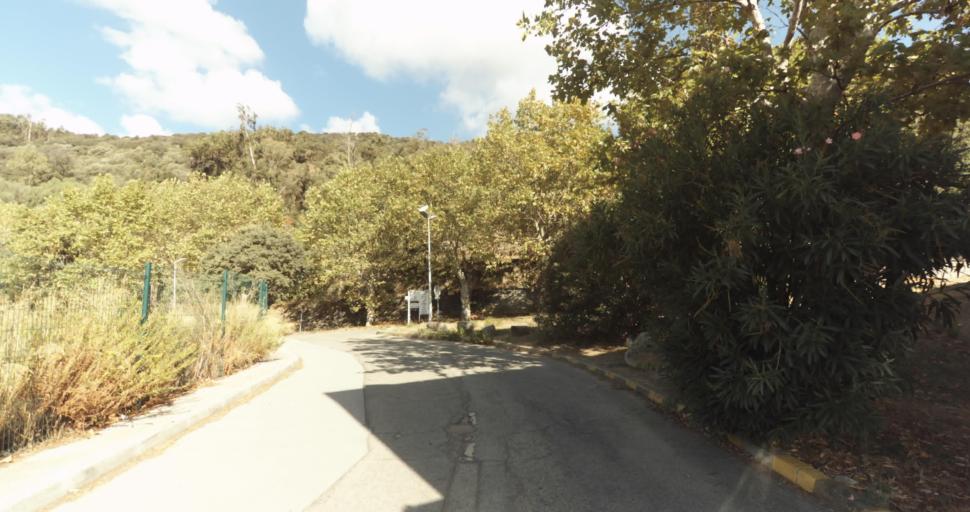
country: FR
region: Corsica
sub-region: Departement de la Corse-du-Sud
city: Ajaccio
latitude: 41.9355
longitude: 8.7145
